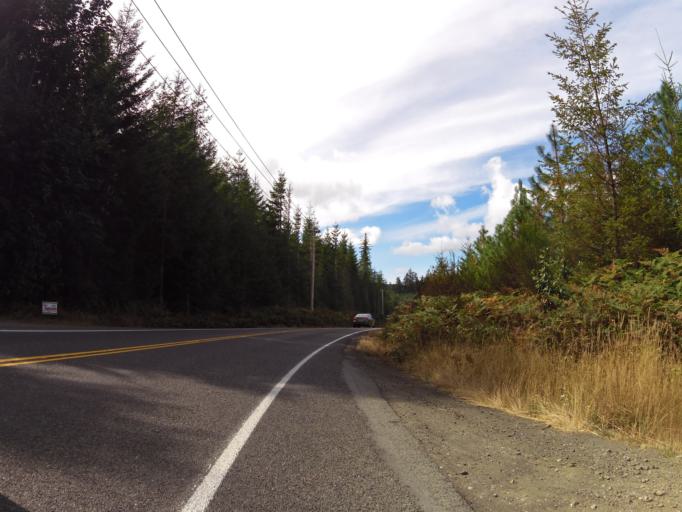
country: US
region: Washington
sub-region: Mason County
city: Shelton
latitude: 47.1469
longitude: -123.0773
